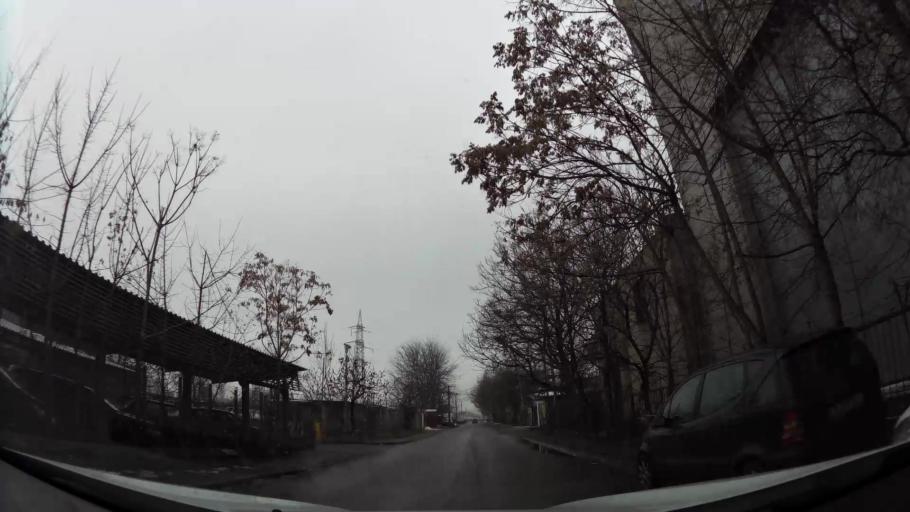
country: RO
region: Ilfov
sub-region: Comuna Popesti-Leordeni
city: Popesti-Leordeni
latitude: 44.4042
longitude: 26.1501
